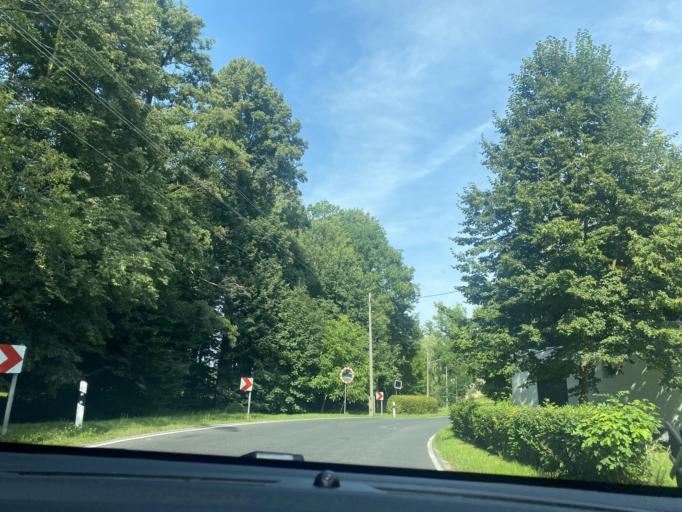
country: DE
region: Saxony
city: Sohland am Rotstein
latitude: 51.1197
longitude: 14.7846
